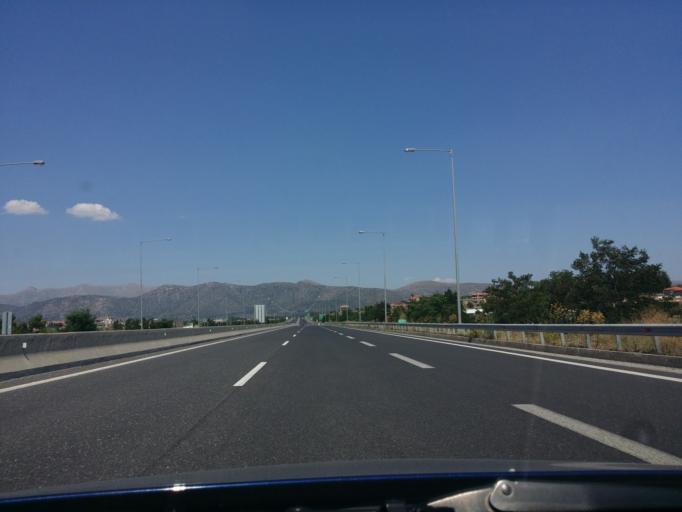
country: GR
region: Peloponnese
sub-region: Nomos Arkadias
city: Tripoli
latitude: 37.4953
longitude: 22.3822
